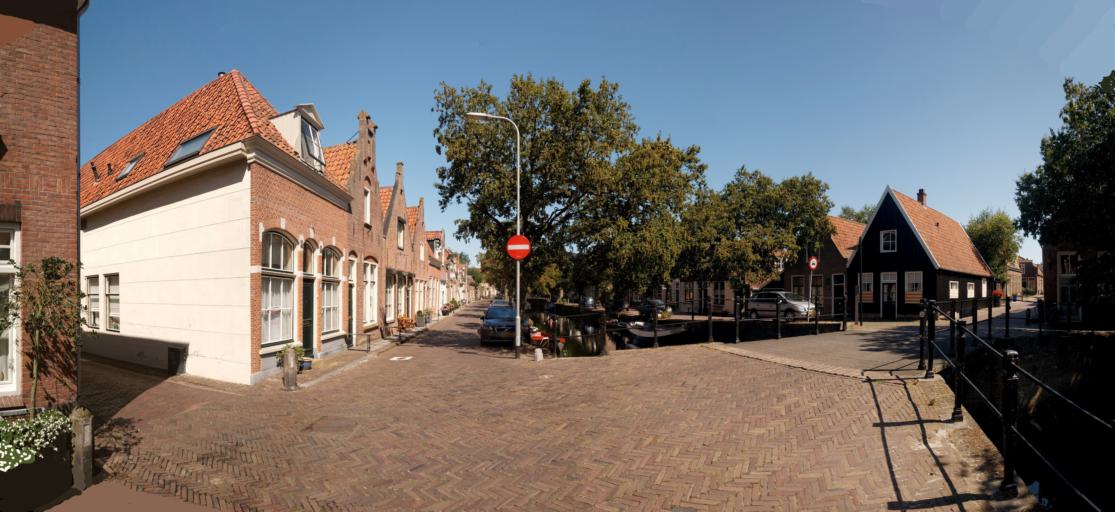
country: NL
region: North Holland
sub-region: Gemeente Enkhuizen
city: Enkhuizen
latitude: 52.7019
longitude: 5.2937
